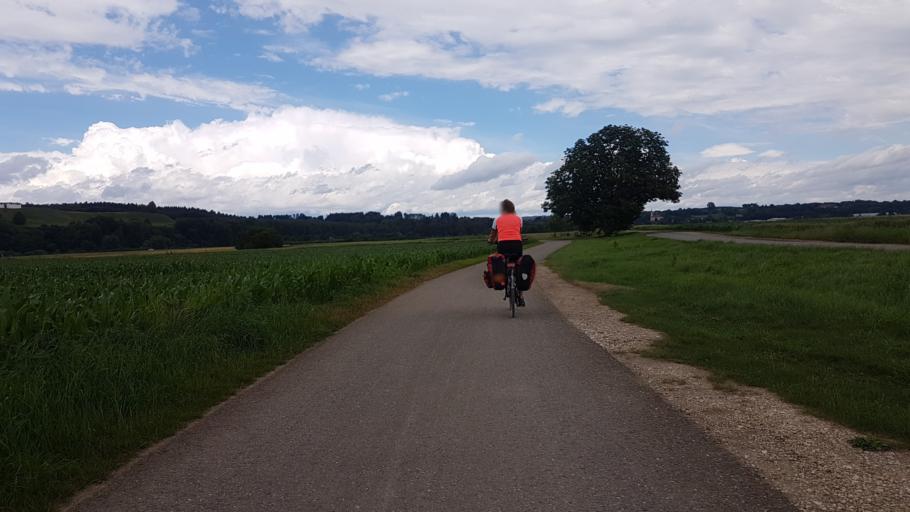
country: DE
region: Baden-Wuerttemberg
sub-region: Tuebingen Region
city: Herbertingen
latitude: 48.0896
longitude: 9.4236
